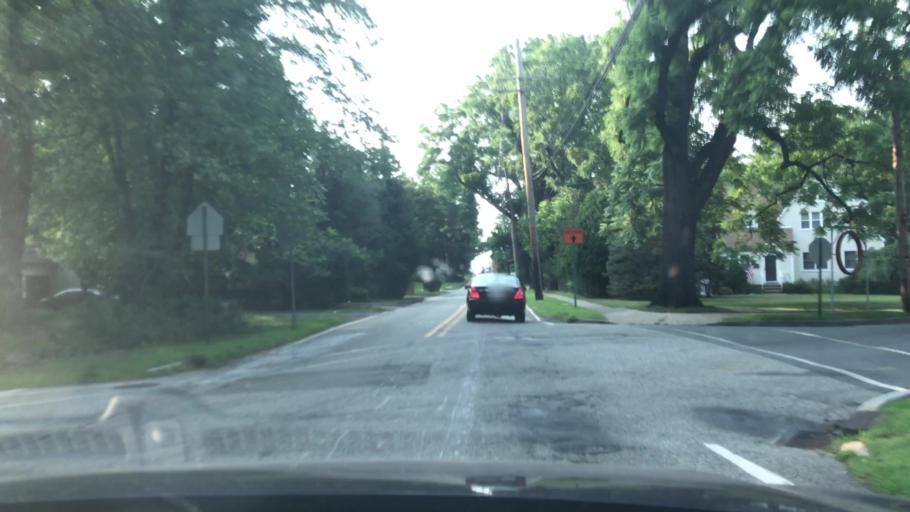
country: US
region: New Jersey
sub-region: Bergen County
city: Norwood
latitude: 40.9919
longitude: -73.9639
